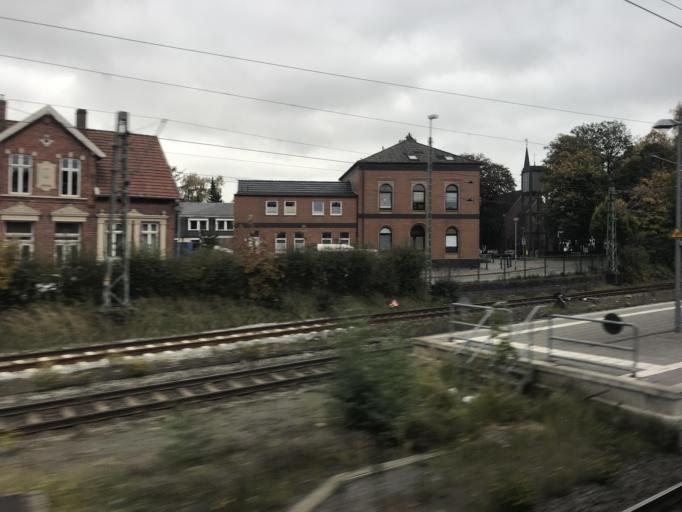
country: DE
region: Lower Saxony
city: Leer
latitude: 53.2324
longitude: 7.4651
